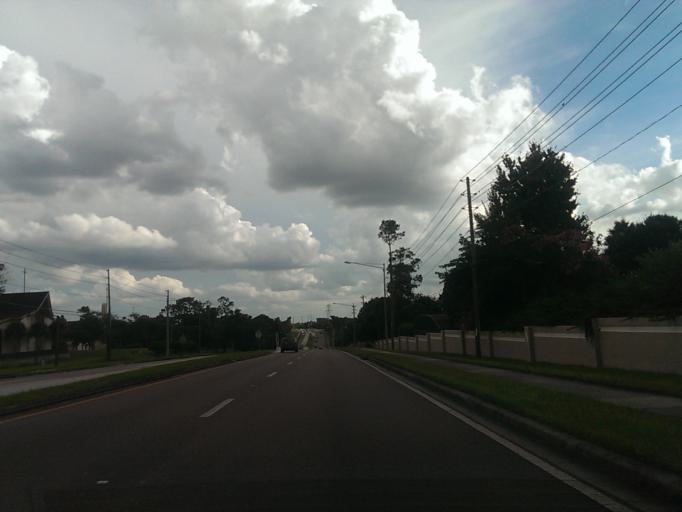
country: US
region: Florida
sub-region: Orange County
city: Bay Hill
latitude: 28.4873
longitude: -81.5086
